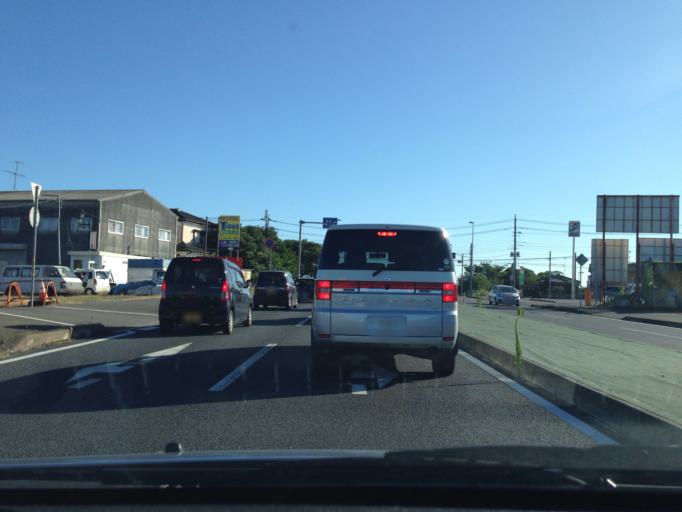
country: JP
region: Ibaraki
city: Naka
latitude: 36.0441
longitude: 140.1823
